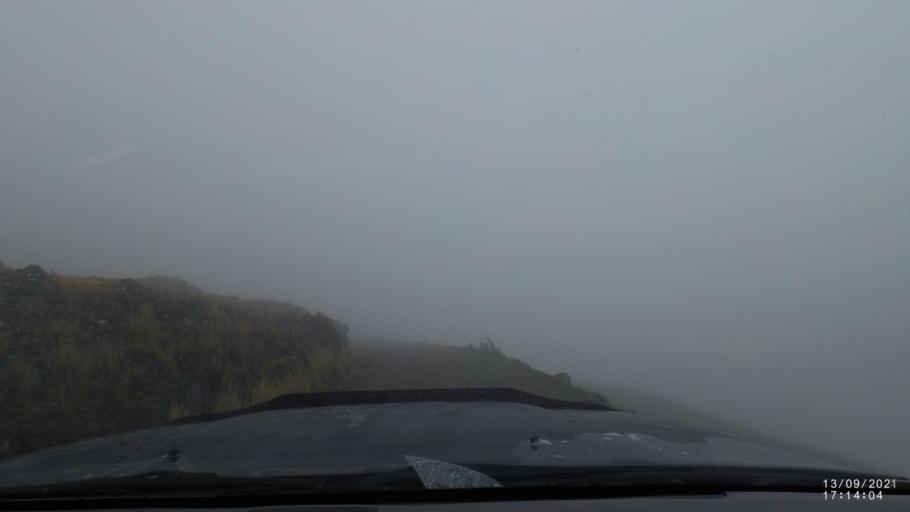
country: BO
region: Cochabamba
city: Colomi
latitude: -17.3416
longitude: -65.7514
